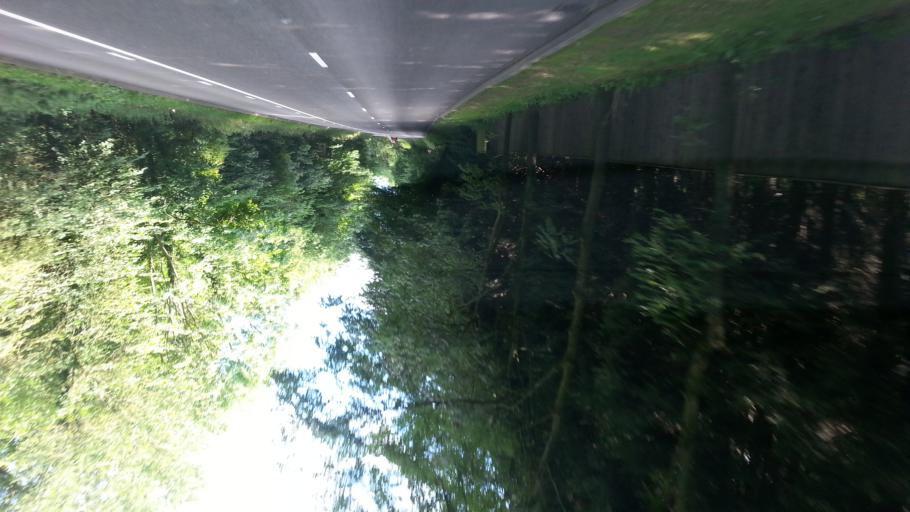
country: GB
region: England
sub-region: Staffordshire
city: Barton under Needwood
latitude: 52.8506
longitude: -1.7725
